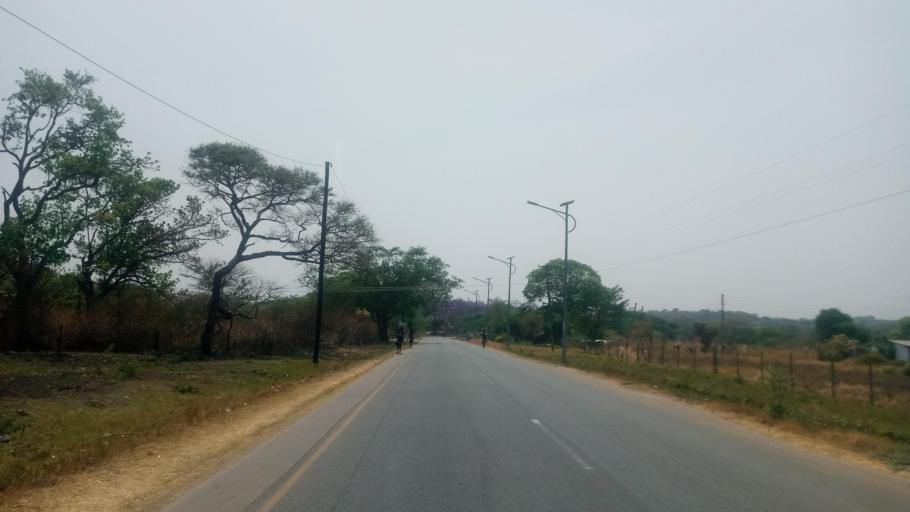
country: ZM
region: Lusaka
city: Lusaka
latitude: -15.4566
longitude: 28.4391
